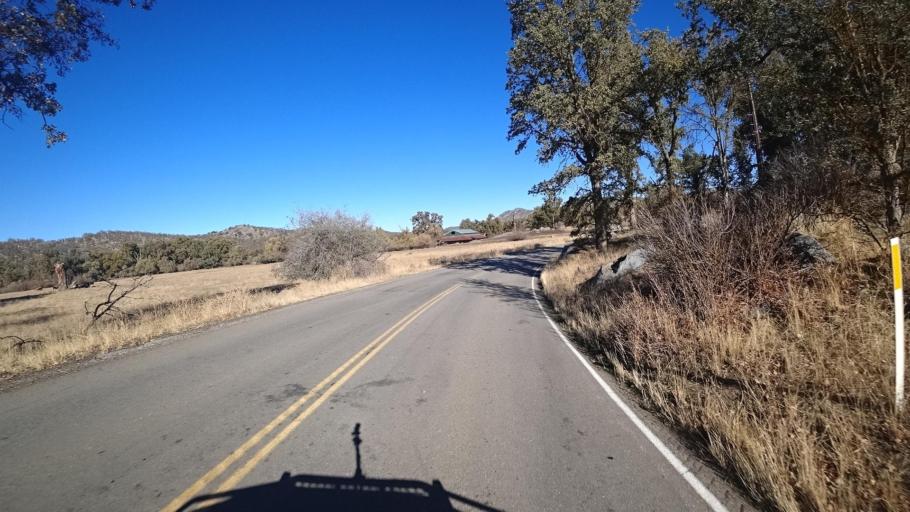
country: US
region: California
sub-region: Kern County
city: Alta Sierra
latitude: 35.7672
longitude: -118.7104
